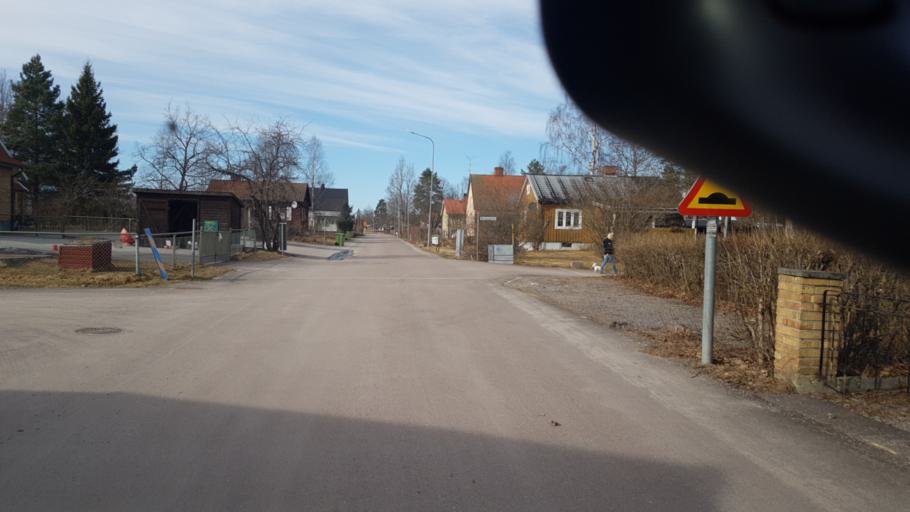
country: SE
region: Vaermland
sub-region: Eda Kommun
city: Charlottenberg
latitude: 59.8856
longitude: 12.3039
